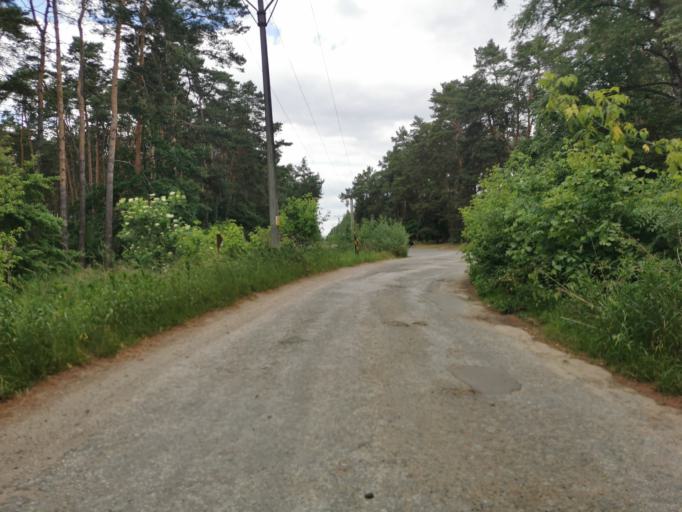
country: CZ
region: South Moravian
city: Bzenec
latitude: 48.9411
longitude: 17.2913
